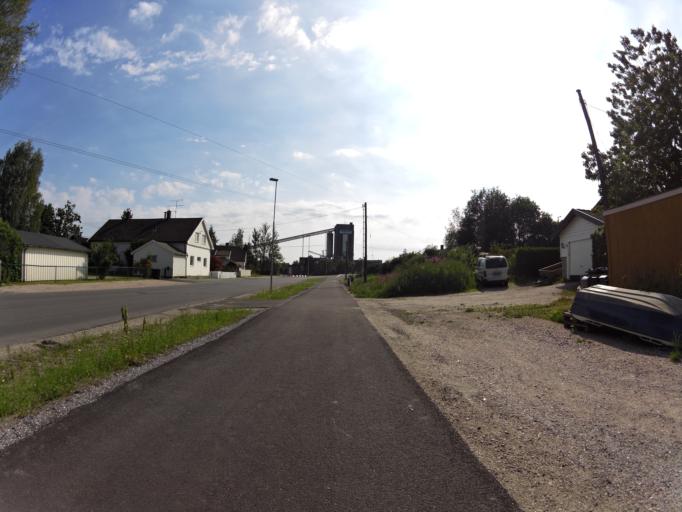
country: NO
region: Ostfold
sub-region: Fredrikstad
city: Fredrikstad
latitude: 59.2327
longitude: 10.9865
